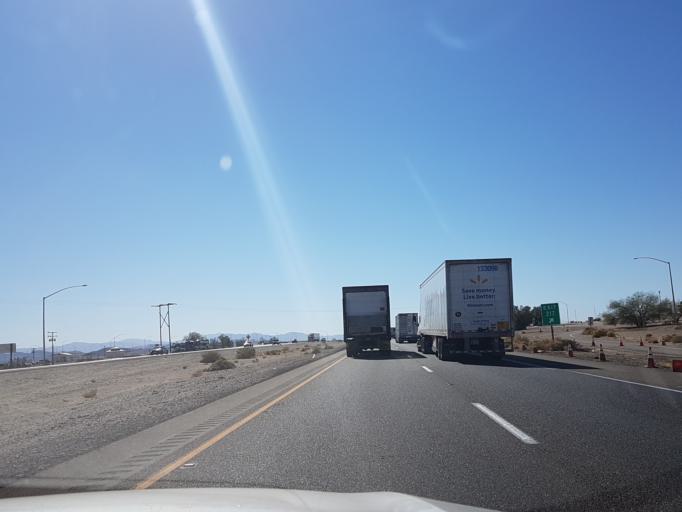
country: US
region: California
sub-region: San Bernardino County
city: Fort Irwin
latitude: 35.0353
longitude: -116.4672
